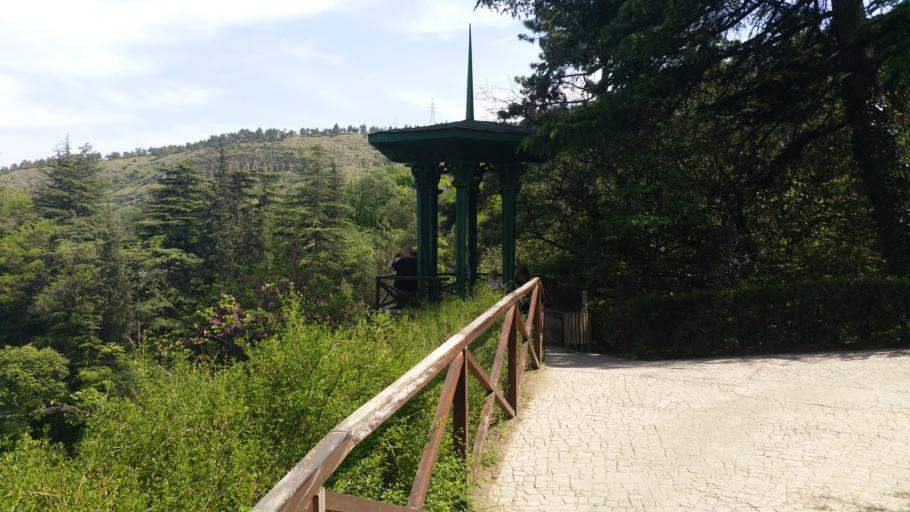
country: GE
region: T'bilisi
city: Tbilisi
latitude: 41.6875
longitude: 44.8019
